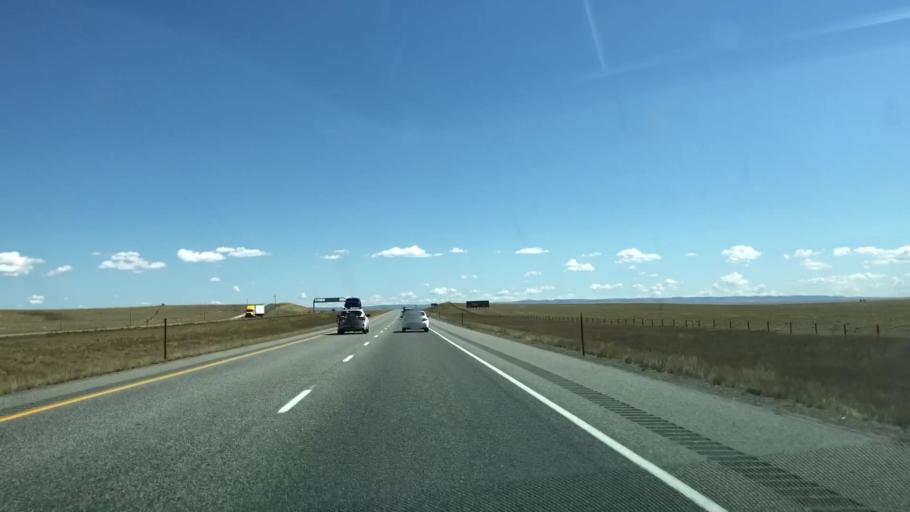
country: US
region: Wyoming
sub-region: Albany County
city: Laramie
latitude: 41.4384
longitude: -105.9321
